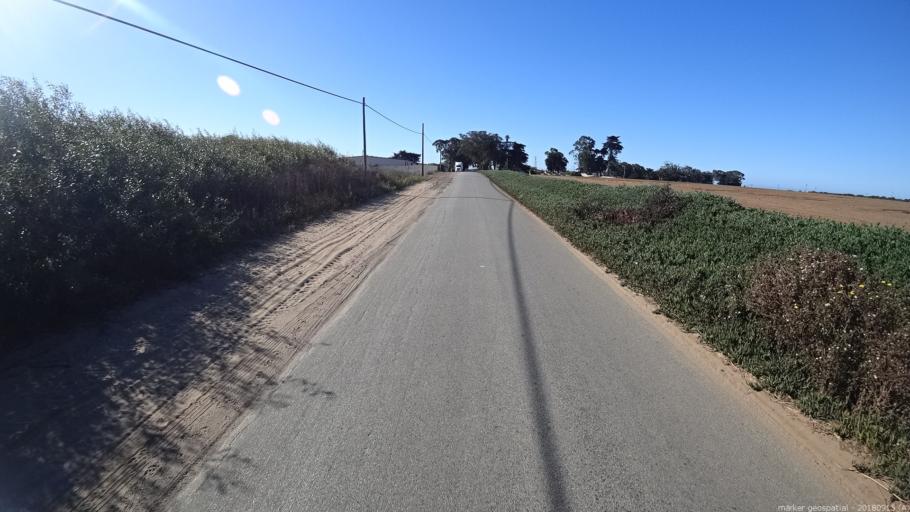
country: US
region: California
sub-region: Monterey County
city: Elkhorn
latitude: 36.8257
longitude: -121.7800
